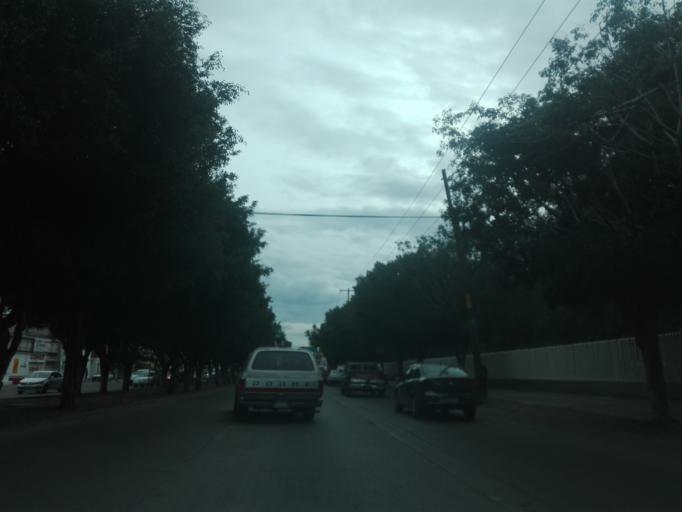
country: MX
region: Guanajuato
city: Leon
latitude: 21.1082
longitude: -101.6570
